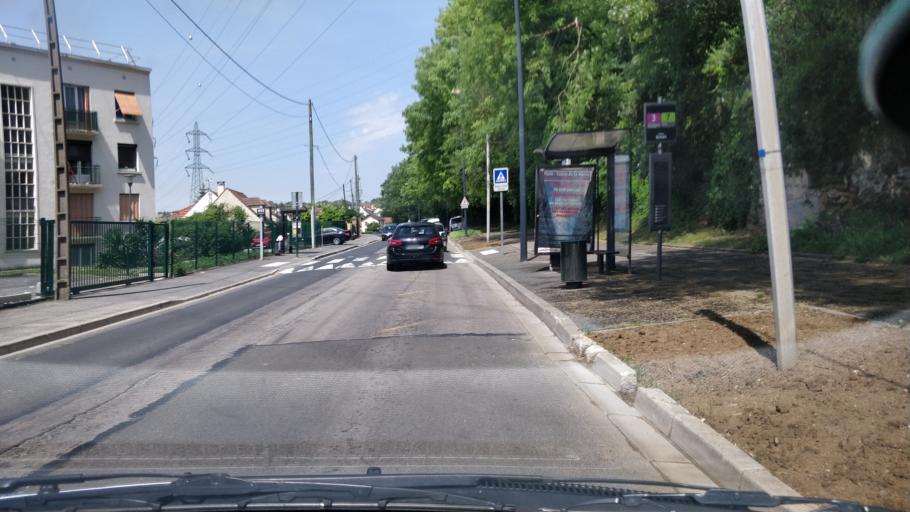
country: FR
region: Ile-de-France
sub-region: Departement de Seine-et-Marne
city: Chelles
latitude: 48.8843
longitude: 2.5890
